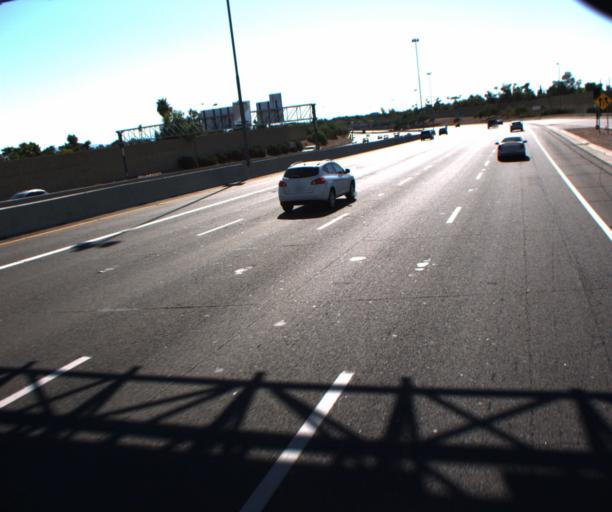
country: US
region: Arizona
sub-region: Maricopa County
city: Guadalupe
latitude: 33.3863
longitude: -111.9580
